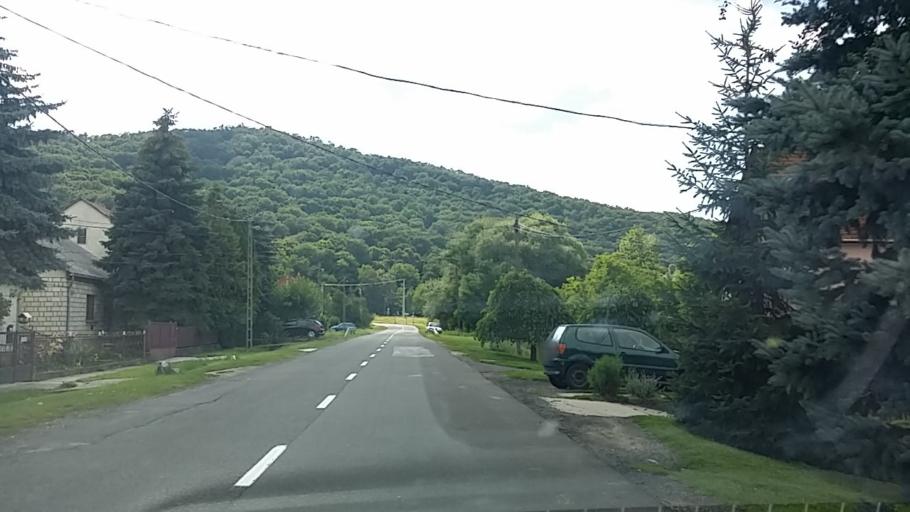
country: SK
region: Nitriansky
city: Sahy
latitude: 48.0483
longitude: 18.9847
